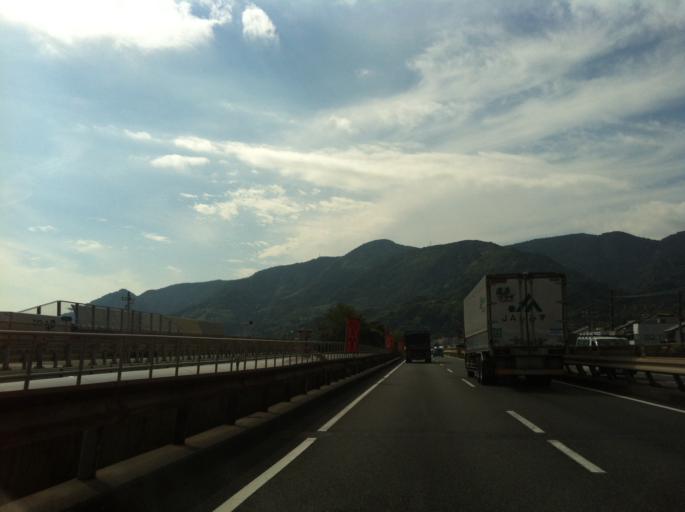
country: JP
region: Shizuoka
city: Fujinomiya
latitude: 35.1055
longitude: 138.5655
